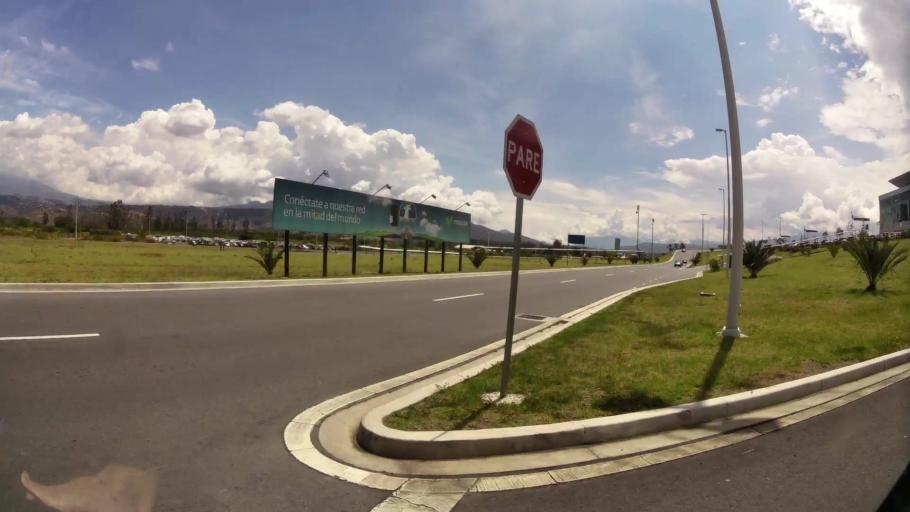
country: EC
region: Pichincha
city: Quito
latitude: -0.1258
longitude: -78.3627
